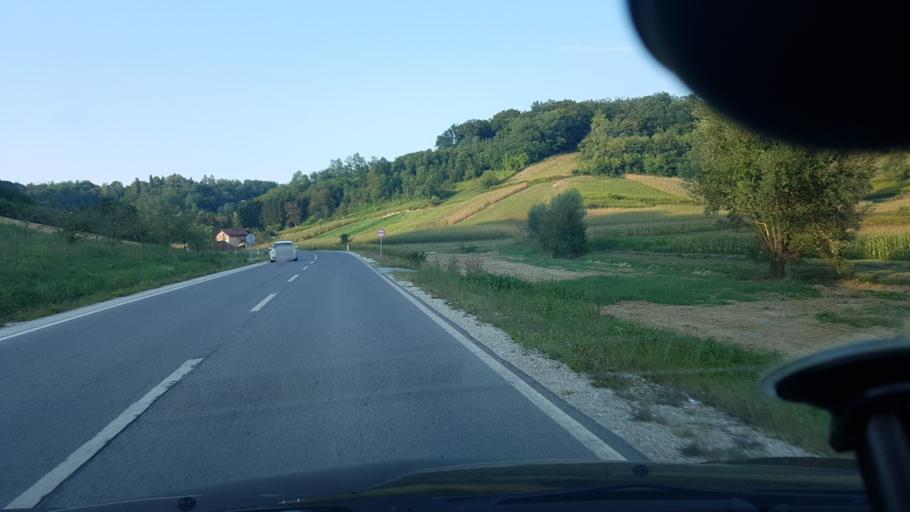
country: HR
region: Krapinsko-Zagorska
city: Pregrada
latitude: 46.1466
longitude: 15.7933
